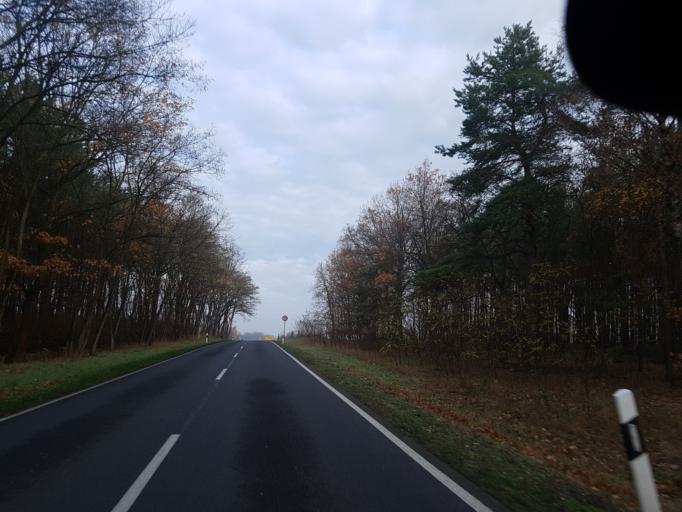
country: DE
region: Saxony-Anhalt
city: Kropstadt
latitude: 51.9563
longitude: 12.7483
